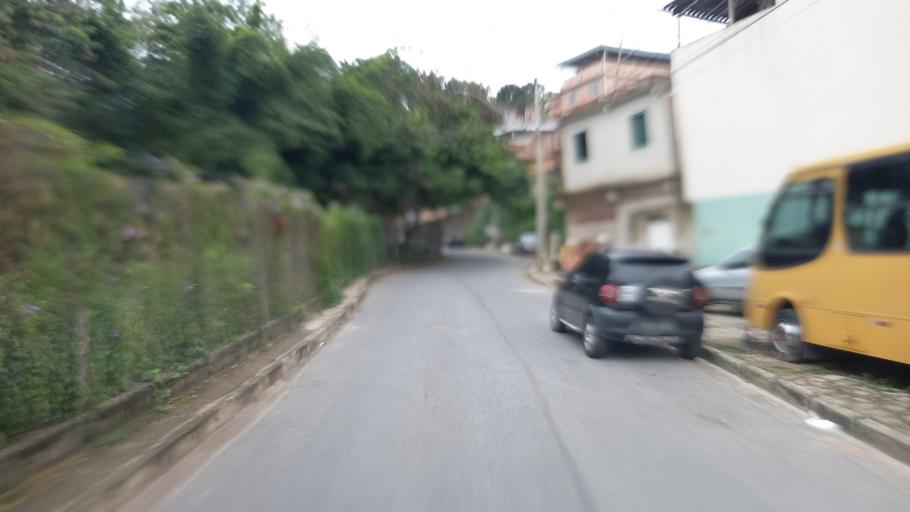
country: BR
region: Minas Gerais
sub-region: Belo Horizonte
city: Belo Horizonte
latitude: -19.9145
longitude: -43.8880
